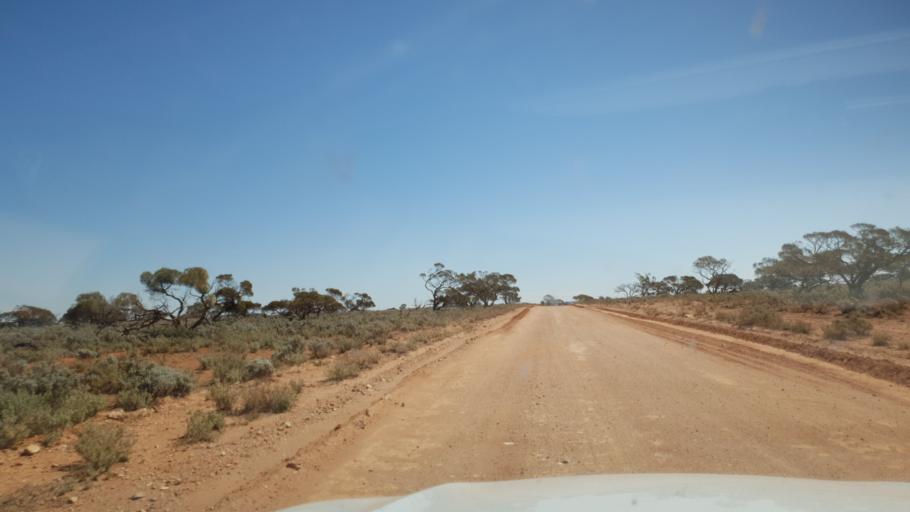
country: AU
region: South Australia
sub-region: Whyalla
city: Whyalla
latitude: -32.6326
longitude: 136.8457
